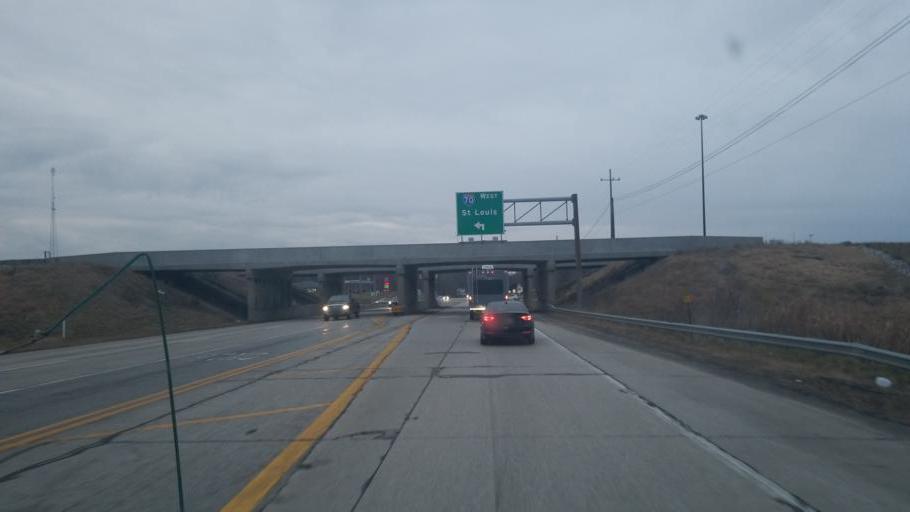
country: US
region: Indiana
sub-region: Clay County
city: Brazil
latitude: 39.4486
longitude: -87.1263
